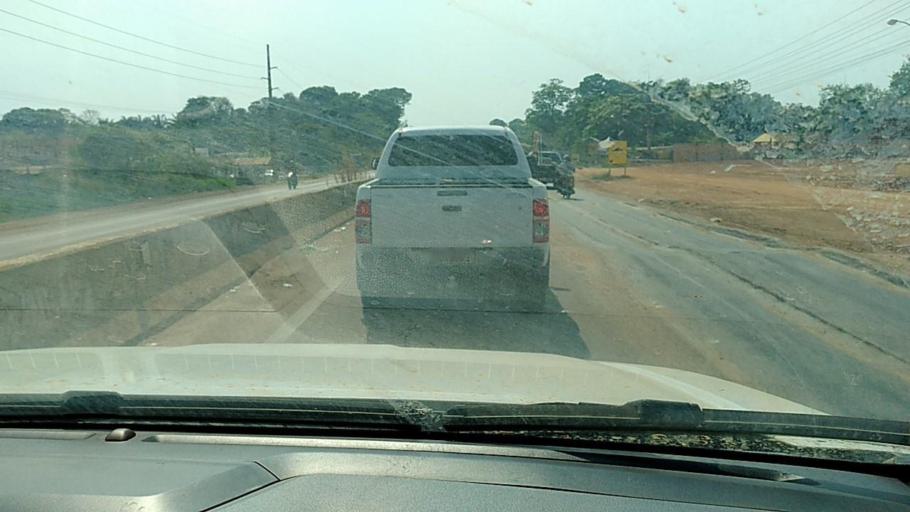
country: BR
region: Rondonia
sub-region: Porto Velho
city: Porto Velho
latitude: -8.7999
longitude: -63.7801
